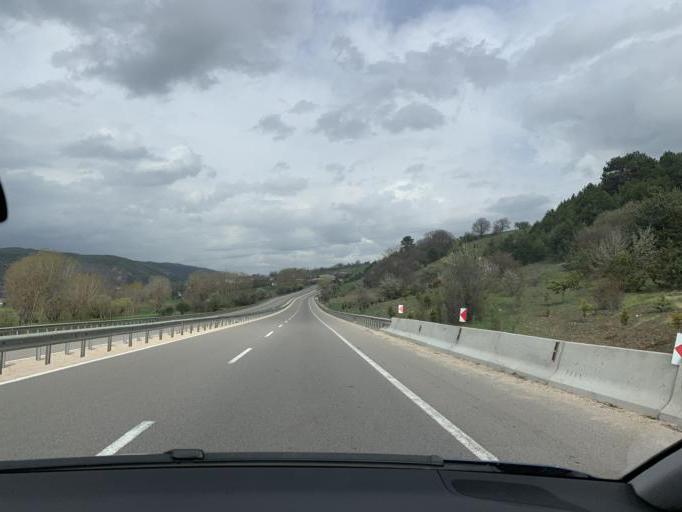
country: TR
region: Bolu
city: Yenicaga
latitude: 40.7861
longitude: 32.1133
